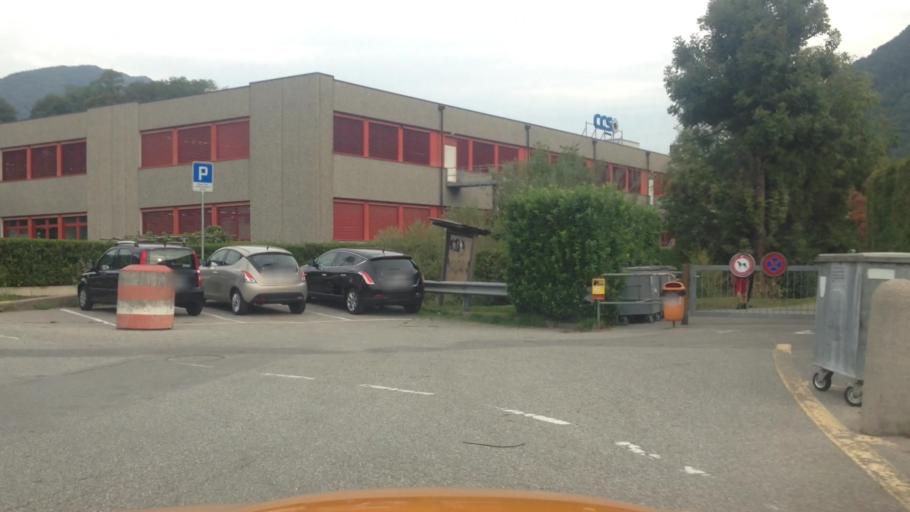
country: CH
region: Ticino
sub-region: Mendrisio District
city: Mendrisio
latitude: 45.8805
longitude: 8.9788
